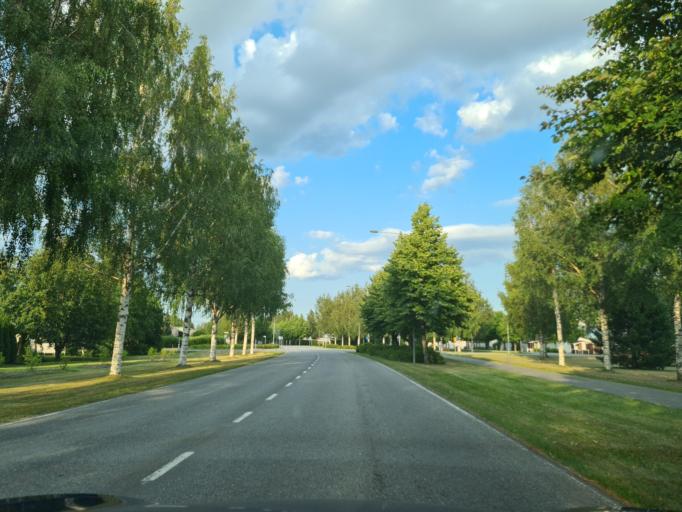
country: FI
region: Southern Ostrobothnia
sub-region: Seinaejoki
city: Lapua
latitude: 62.9682
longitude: 22.9862
